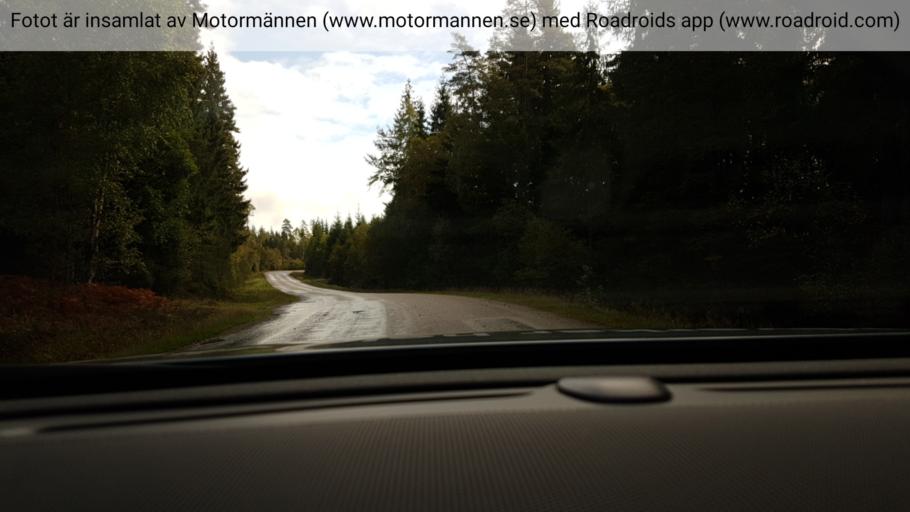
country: SE
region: Vaestra Goetaland
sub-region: Marks Kommun
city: Fritsla
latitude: 57.4018
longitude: 12.8631
